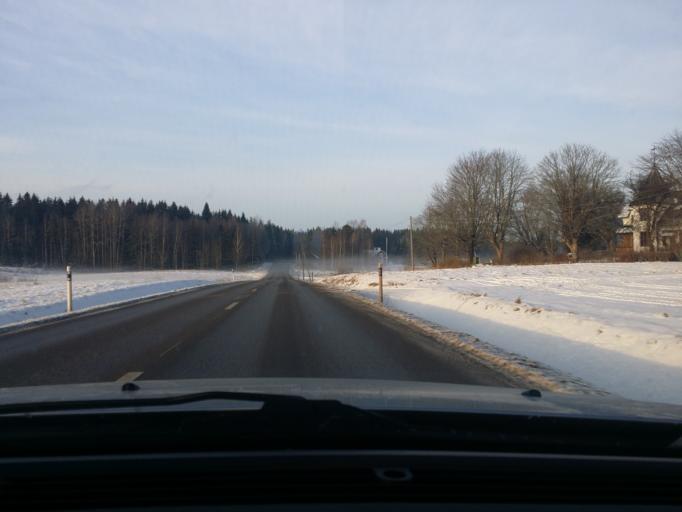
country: SE
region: OErebro
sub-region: Lindesbergs Kommun
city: Frovi
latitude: 59.5187
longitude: 15.3266
